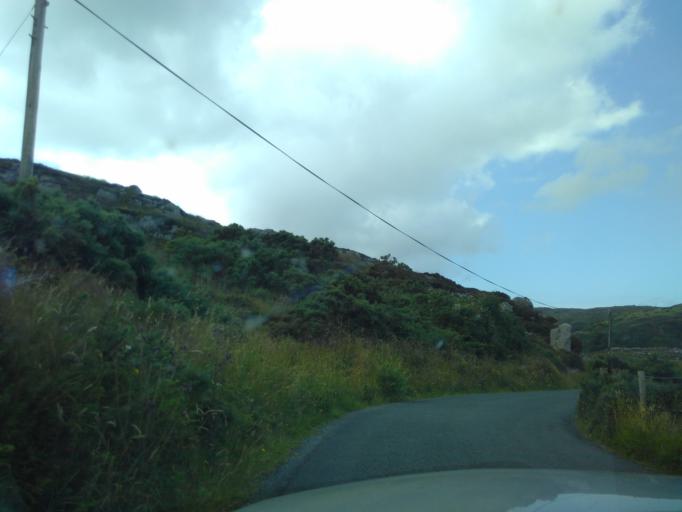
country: IE
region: Ulster
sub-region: County Donegal
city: Ramelton
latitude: 55.2231
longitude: -7.6169
